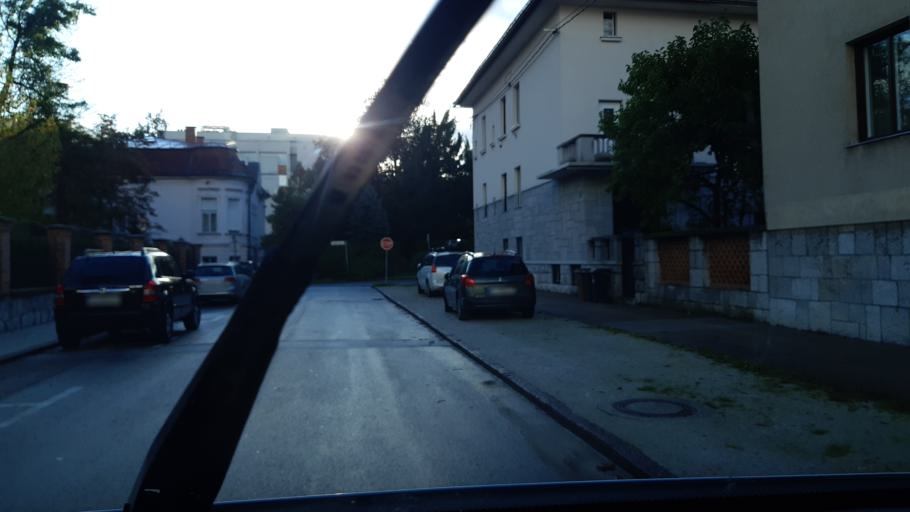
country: SI
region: Ljubljana
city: Ljubljana
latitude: 46.0484
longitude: 14.5149
